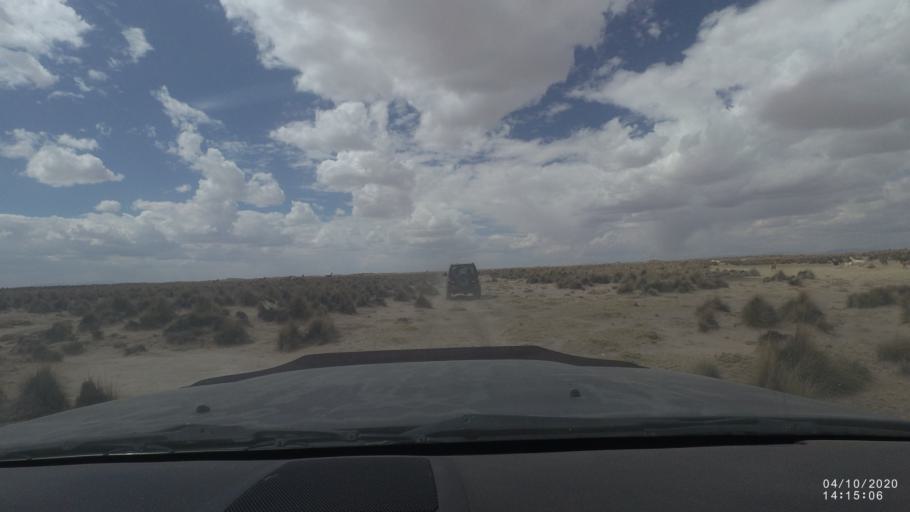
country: BO
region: Oruro
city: Poopo
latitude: -18.6938
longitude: -67.4542
